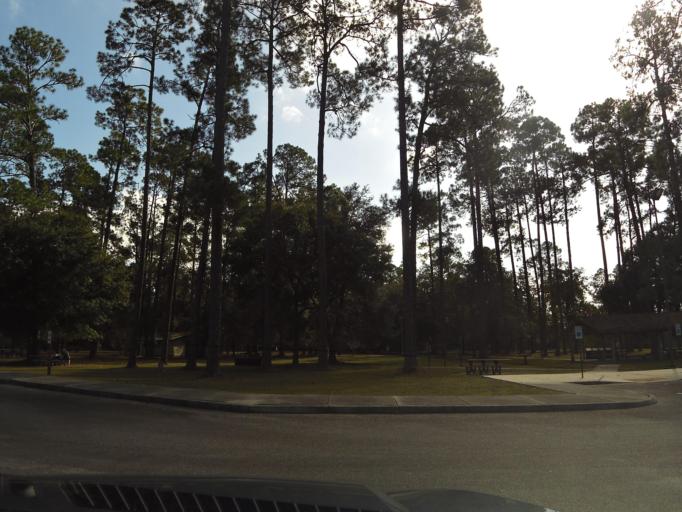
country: US
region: Georgia
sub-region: Charlton County
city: Folkston
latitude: 30.7392
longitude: -82.1395
